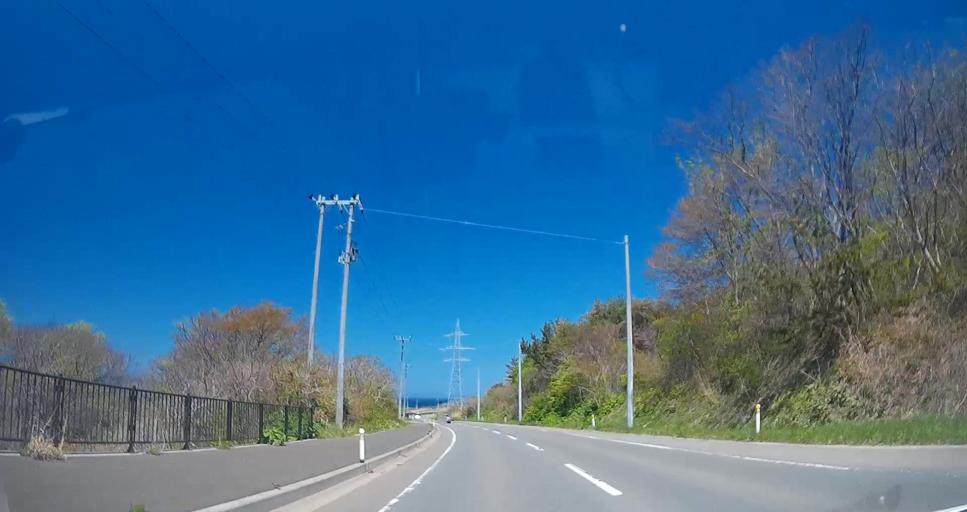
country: JP
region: Aomori
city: Mutsu
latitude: 41.3953
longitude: 141.4222
